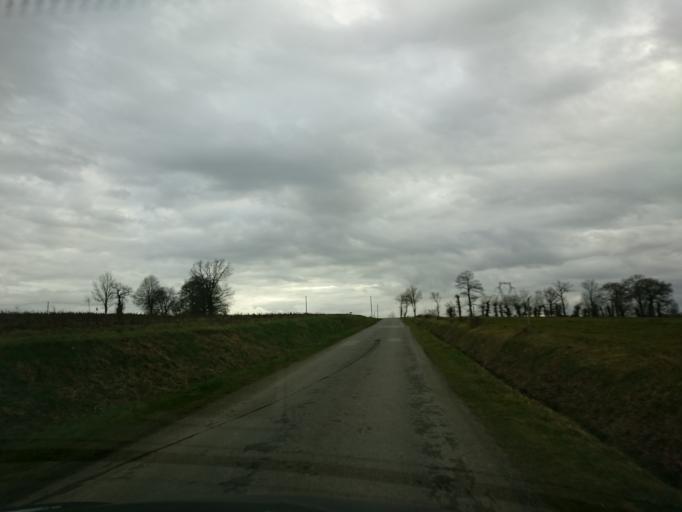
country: FR
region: Brittany
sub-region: Departement d'Ille-et-Vilaine
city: Crevin
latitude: 47.9117
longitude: -1.6376
